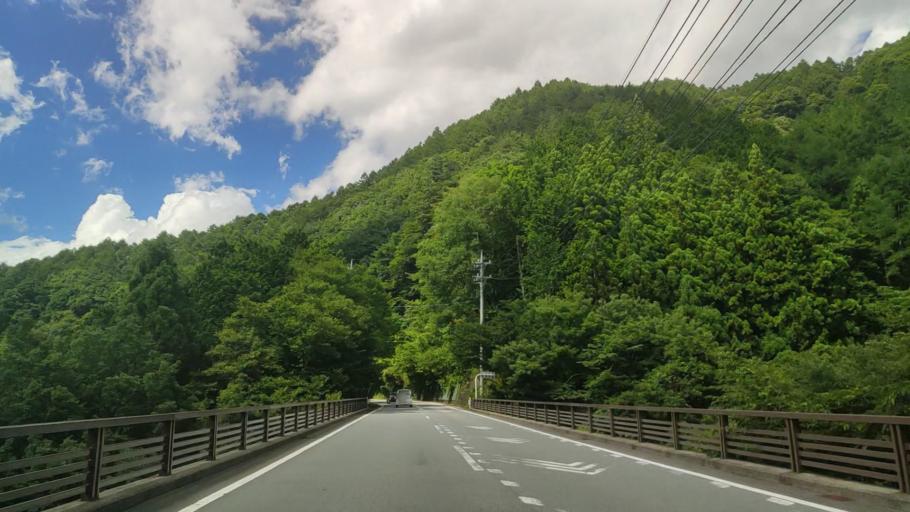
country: JP
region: Yamanashi
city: Enzan
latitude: 35.8378
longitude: 138.7668
